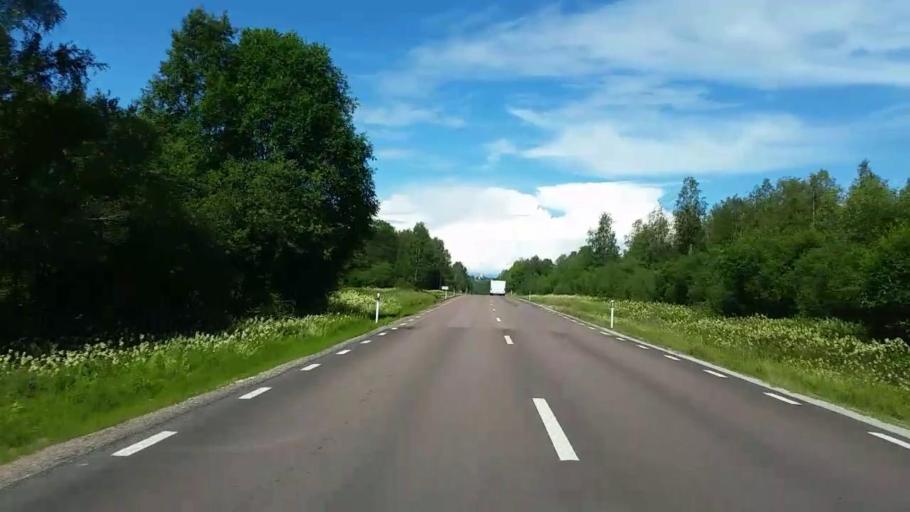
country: SE
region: Dalarna
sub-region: Rattviks Kommun
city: Raettvik
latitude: 60.9811
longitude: 15.2236
